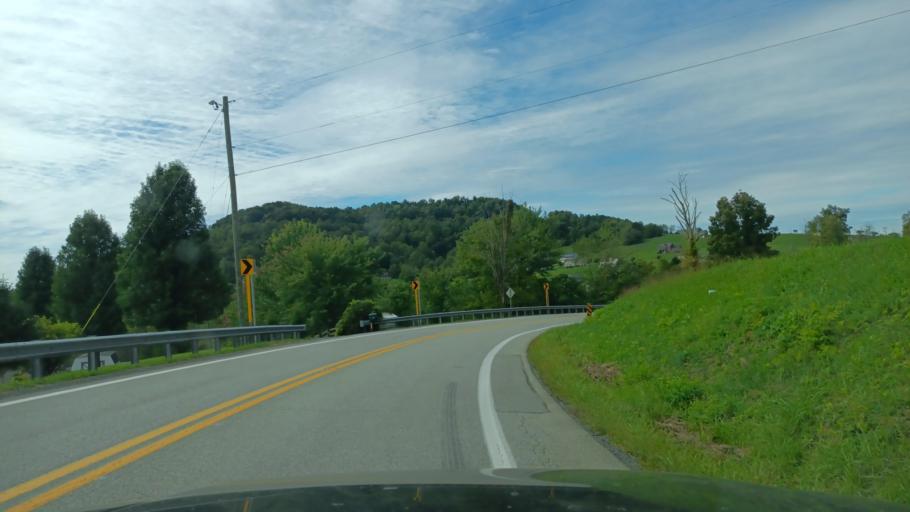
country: US
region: West Virginia
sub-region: Harrison County
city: Bridgeport
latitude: 39.3000
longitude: -80.1737
